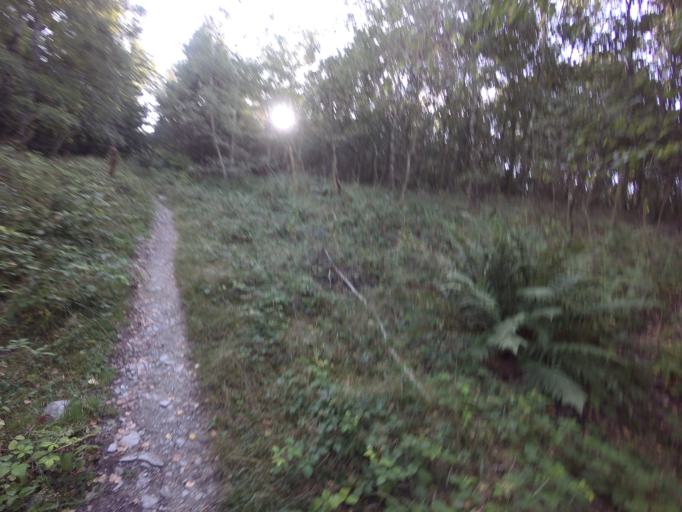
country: DE
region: North Rhine-Westphalia
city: Heimbach
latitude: 50.6115
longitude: 6.3988
